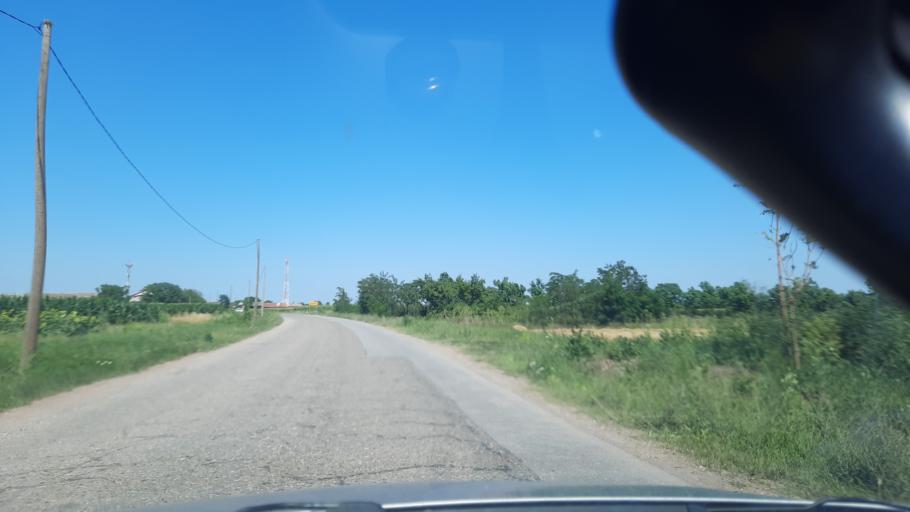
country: RS
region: Central Serbia
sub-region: Podunavski Okrug
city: Smederevo
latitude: 44.5909
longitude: 20.9810
